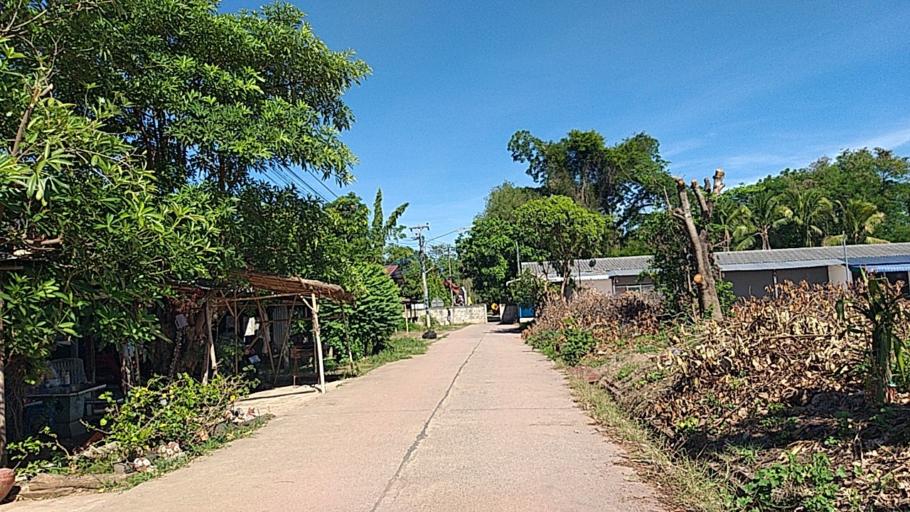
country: TH
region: Chaiyaphum
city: Ban Thaen
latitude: 16.4068
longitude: 102.3512
